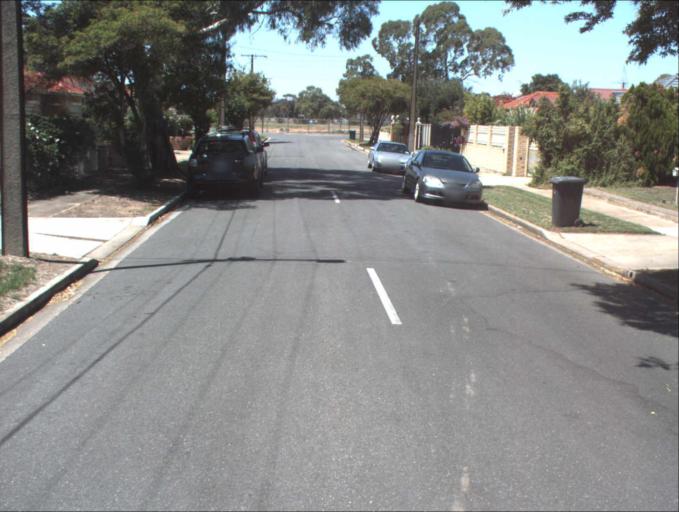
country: AU
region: South Australia
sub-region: Charles Sturt
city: Woodville North
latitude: -34.8521
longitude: 138.5530
